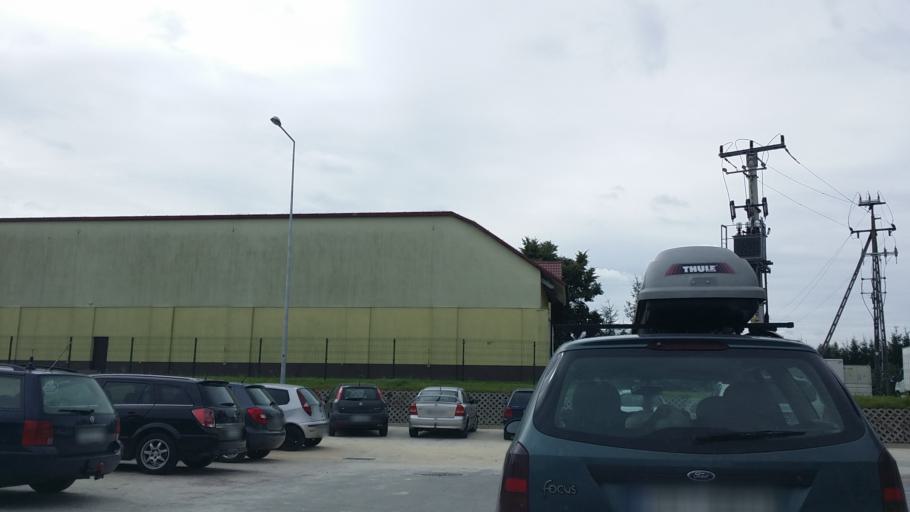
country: PL
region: Lesser Poland Voivodeship
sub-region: Powiat oswiecimski
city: Zator
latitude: 49.9965
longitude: 19.4316
